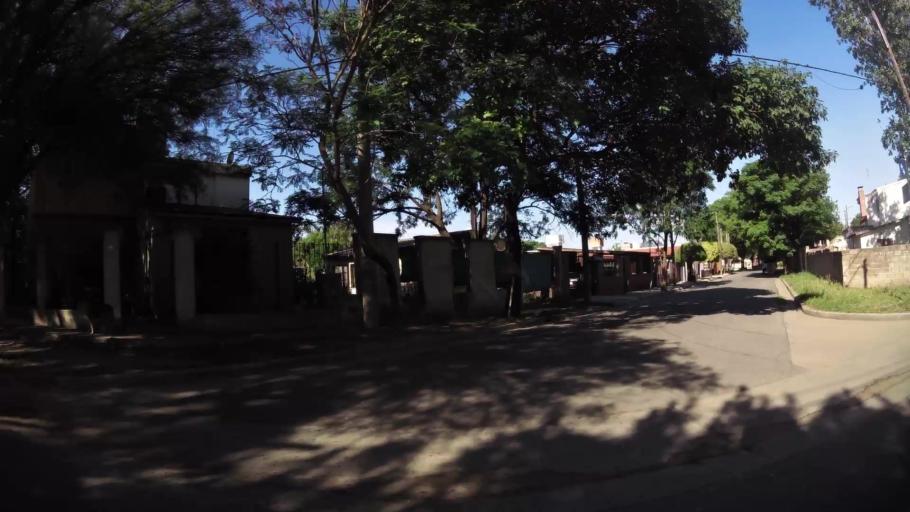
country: AR
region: Cordoba
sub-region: Departamento de Capital
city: Cordoba
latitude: -31.3582
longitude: -64.1909
